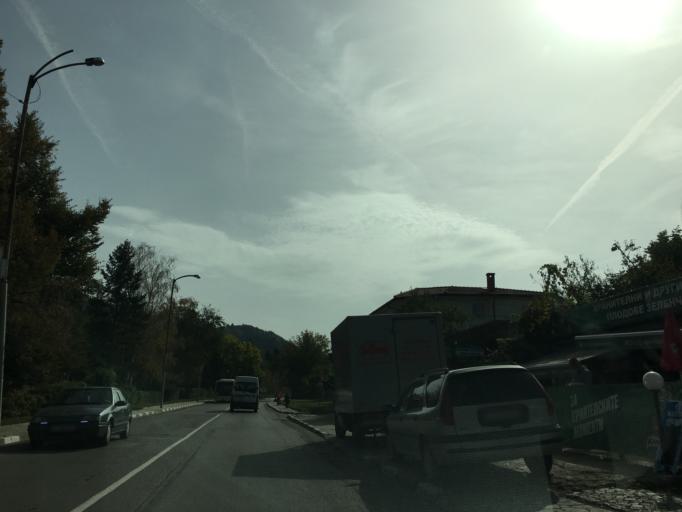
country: BG
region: Sofia-Capital
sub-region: Stolichna Obshtina
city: Sofia
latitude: 42.5852
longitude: 23.4219
